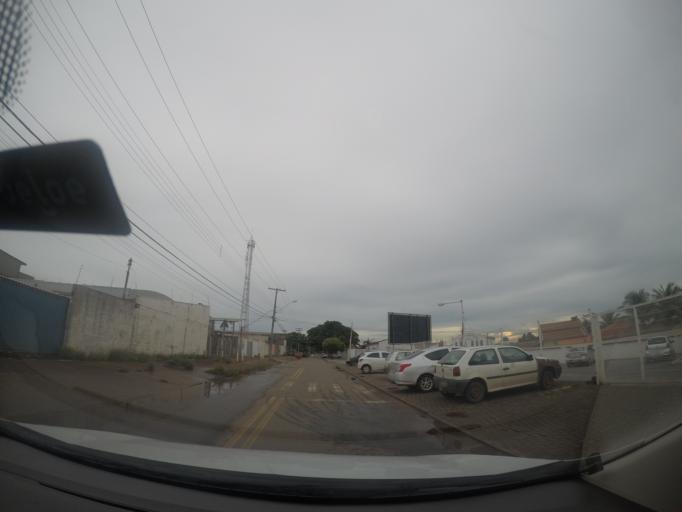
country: BR
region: Goias
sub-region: Goiania
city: Goiania
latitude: -16.6297
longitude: -49.2354
